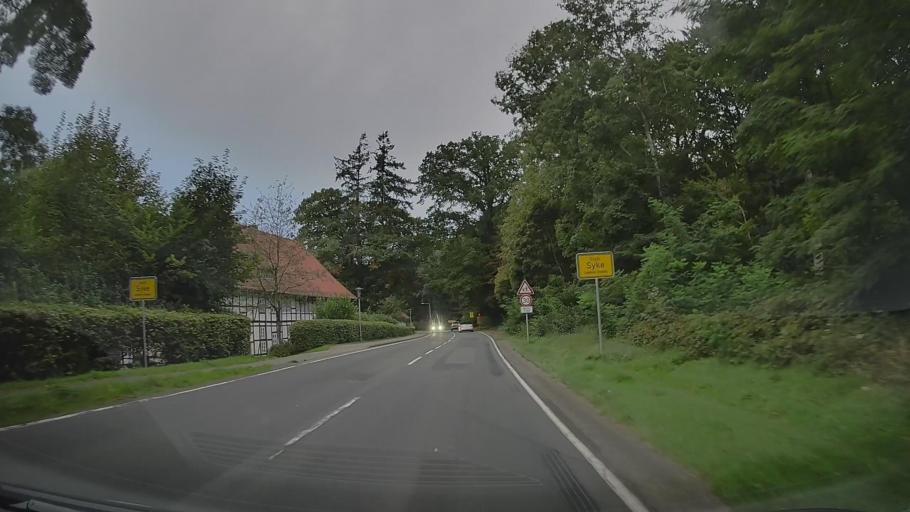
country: DE
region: Lower Saxony
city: Syke
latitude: 52.9130
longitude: 8.8437
